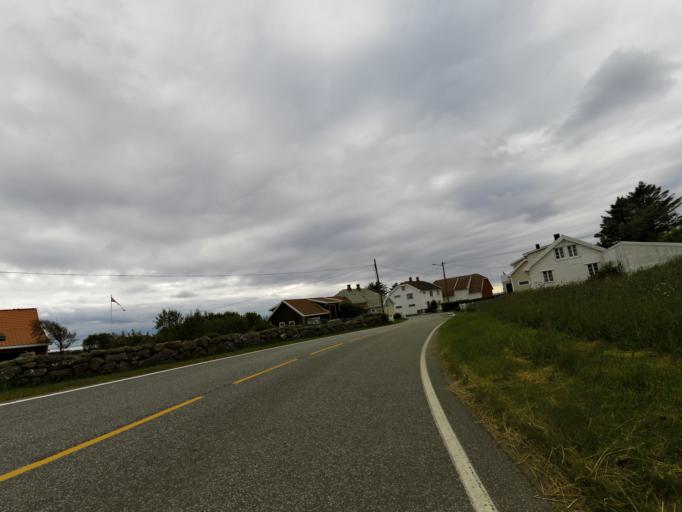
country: NO
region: Vest-Agder
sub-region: Farsund
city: Vestbygd
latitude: 58.1249
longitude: 6.6086
